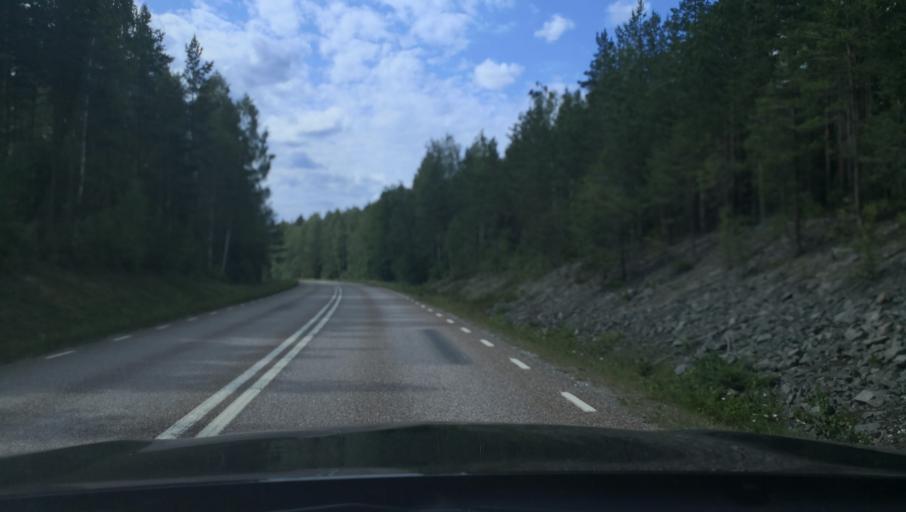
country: SE
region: Dalarna
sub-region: Avesta Kommun
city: Avesta
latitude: 59.9793
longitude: 16.1410
